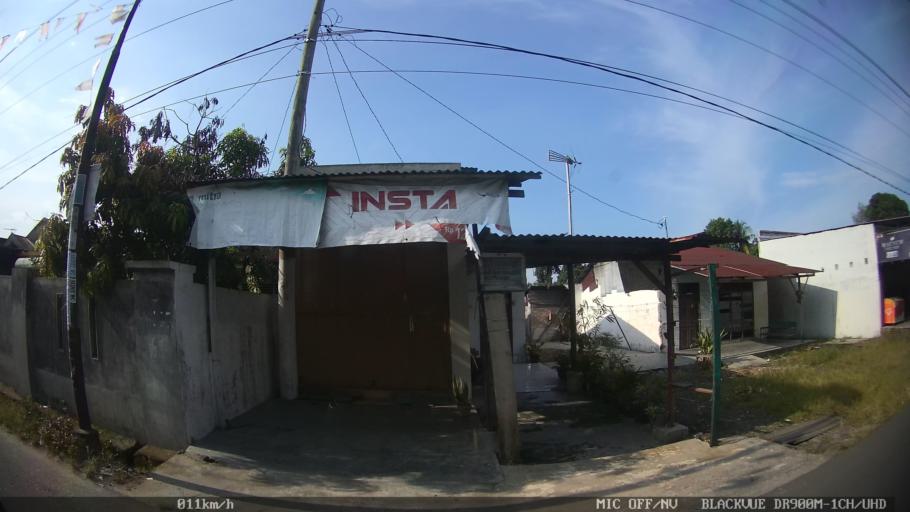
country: ID
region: North Sumatra
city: Medan
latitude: 3.5942
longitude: 98.7653
